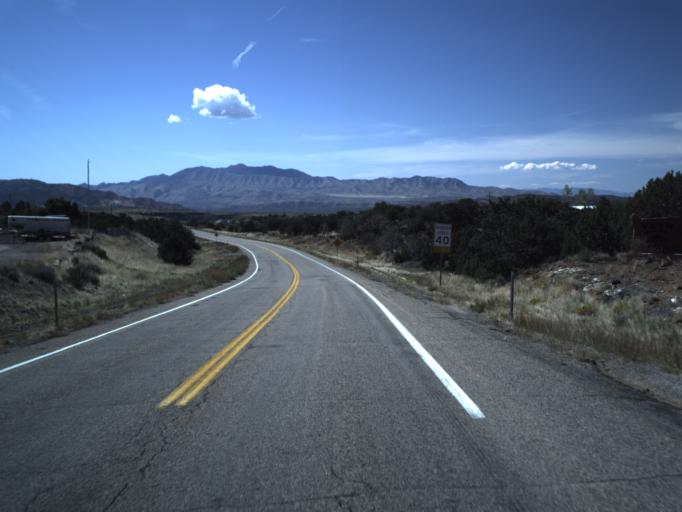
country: US
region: Utah
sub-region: Washington County
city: Ivins
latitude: 37.3491
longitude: -113.6894
